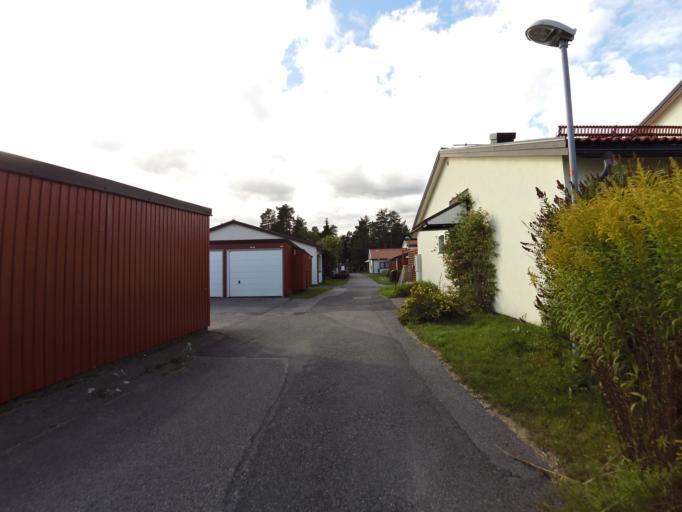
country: SE
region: Gaevleborg
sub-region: Gavle Kommun
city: Gavle
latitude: 60.6657
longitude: 17.2220
